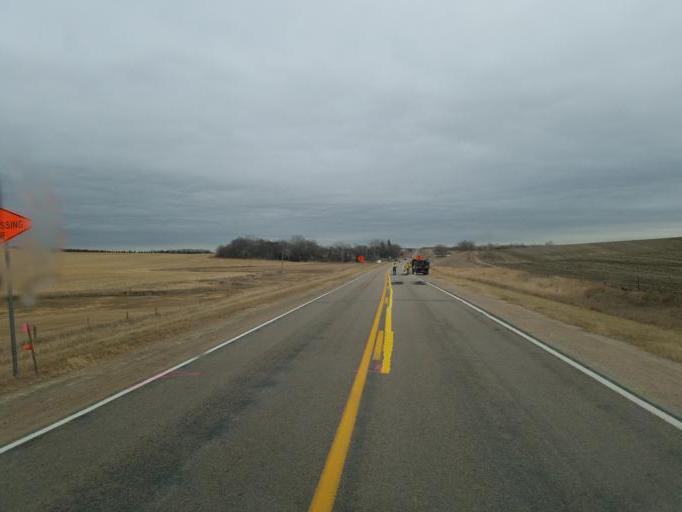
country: US
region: Nebraska
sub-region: Cedar County
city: Hartington
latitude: 42.6127
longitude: -97.4359
